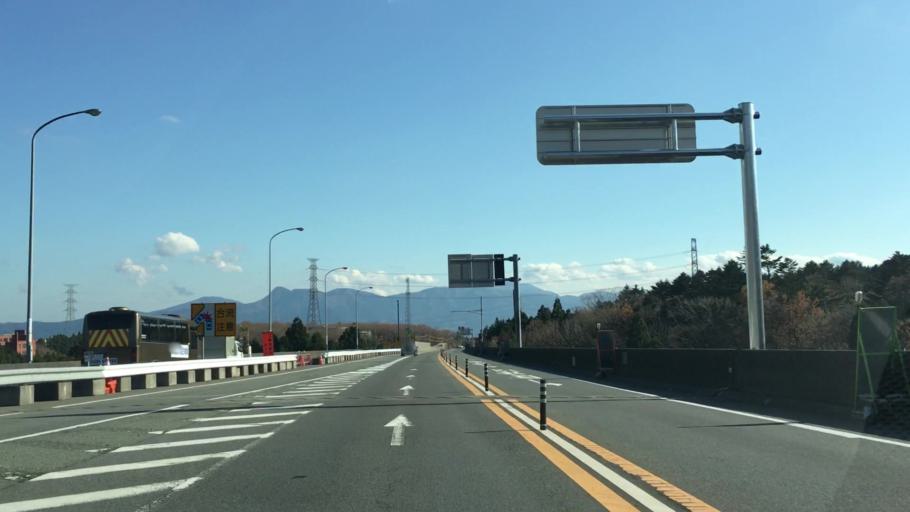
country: JP
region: Shizuoka
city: Gotemba
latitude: 35.3592
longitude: 138.8675
